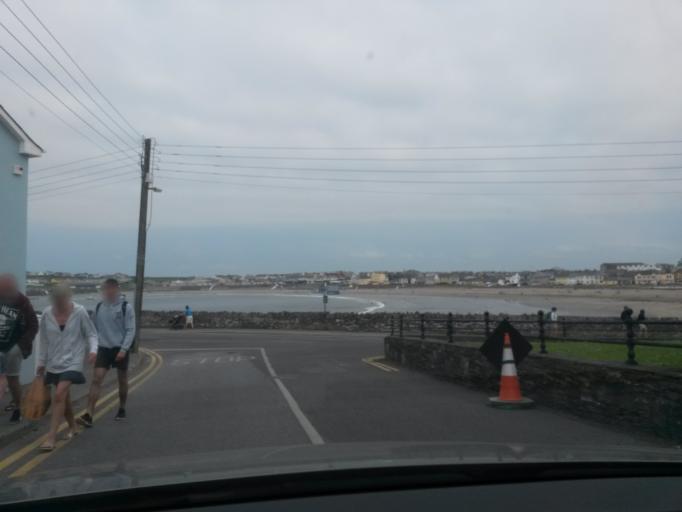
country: IE
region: Munster
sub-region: Ciarrai
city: Ballybunnion
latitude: 52.6795
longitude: -9.6563
